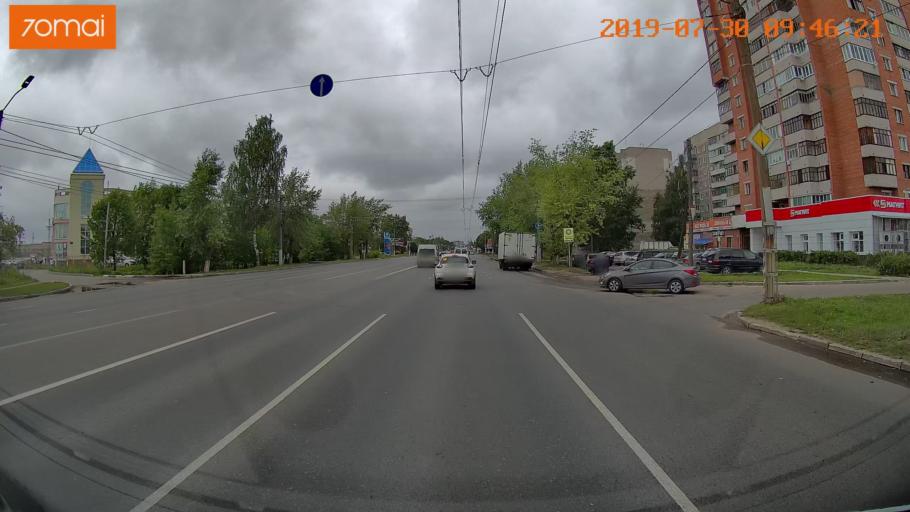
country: RU
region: Ivanovo
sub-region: Gorod Ivanovo
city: Ivanovo
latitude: 56.9546
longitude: 40.9747
